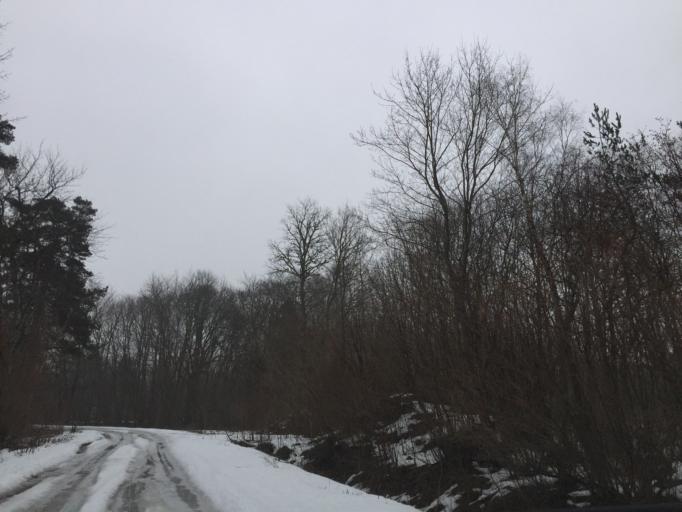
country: EE
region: Saare
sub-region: Kuressaare linn
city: Kuressaare
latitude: 58.2739
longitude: 22.5664
